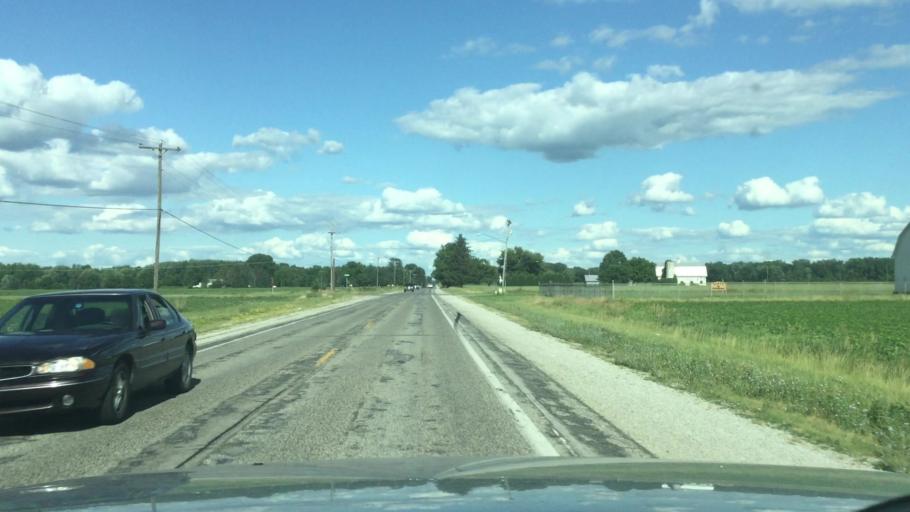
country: US
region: Michigan
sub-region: Saginaw County
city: Shields
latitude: 43.3798
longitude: -84.1131
